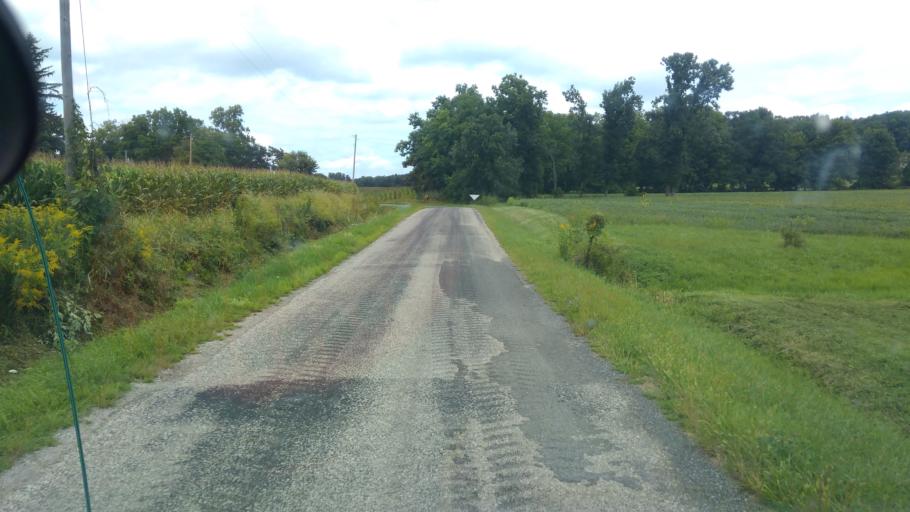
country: US
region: Ohio
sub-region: Richland County
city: Lincoln Heights
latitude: 40.8283
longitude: -82.4069
